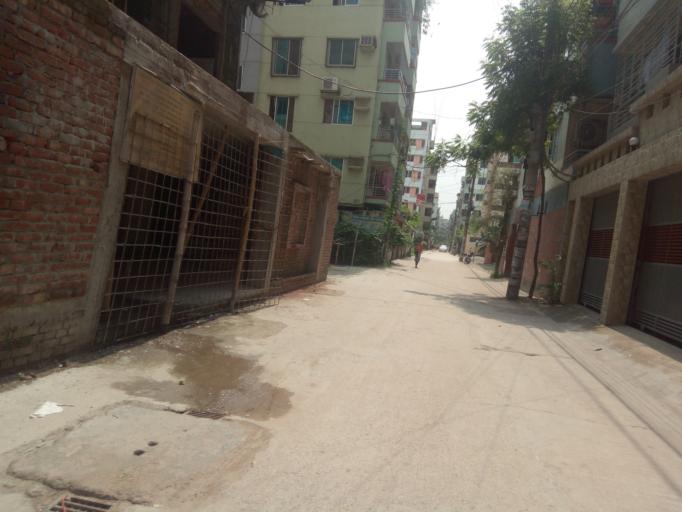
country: BD
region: Dhaka
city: Paltan
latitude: 23.7616
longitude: 90.4399
